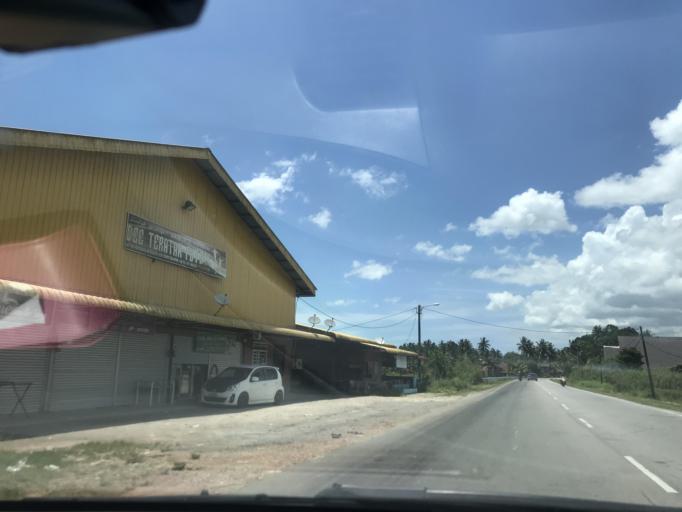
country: MY
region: Kelantan
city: Tumpat
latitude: 6.1949
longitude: 102.1388
